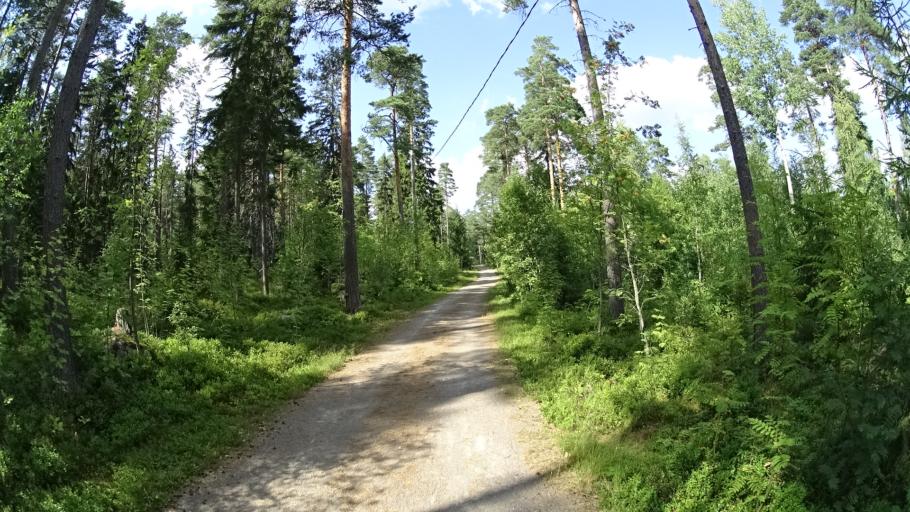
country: FI
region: Uusimaa
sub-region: Porvoo
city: Porvoo
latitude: 60.3848
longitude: 25.6832
